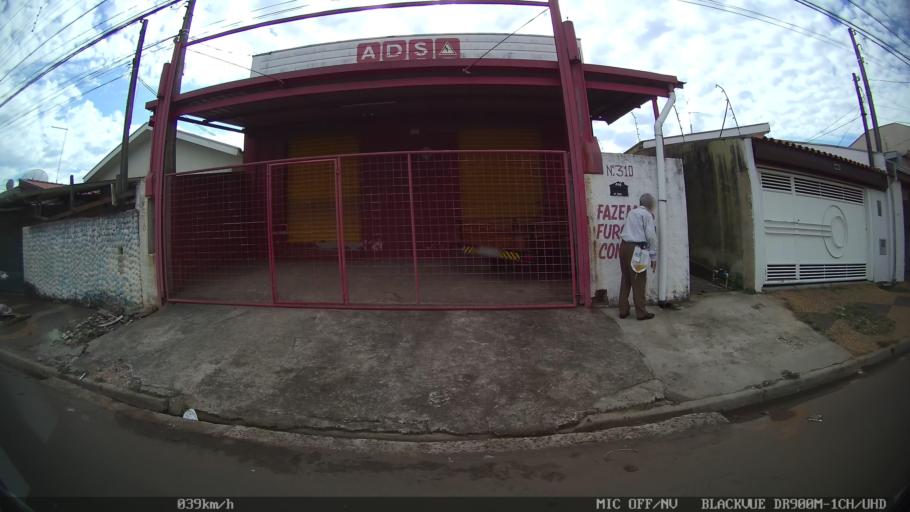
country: BR
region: Sao Paulo
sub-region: Americana
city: Americana
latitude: -22.7419
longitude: -47.3592
